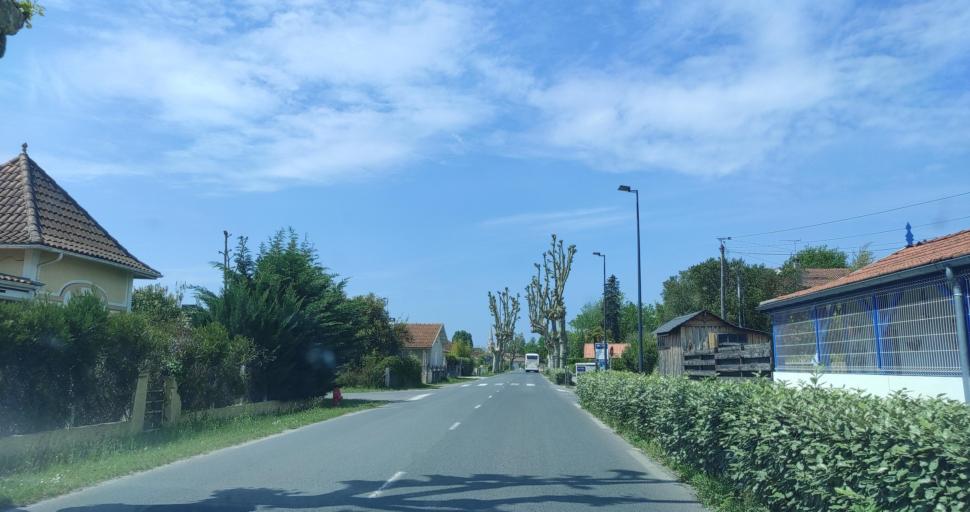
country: FR
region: Aquitaine
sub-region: Departement de la Gironde
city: Ares
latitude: 44.7634
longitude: -1.1336
